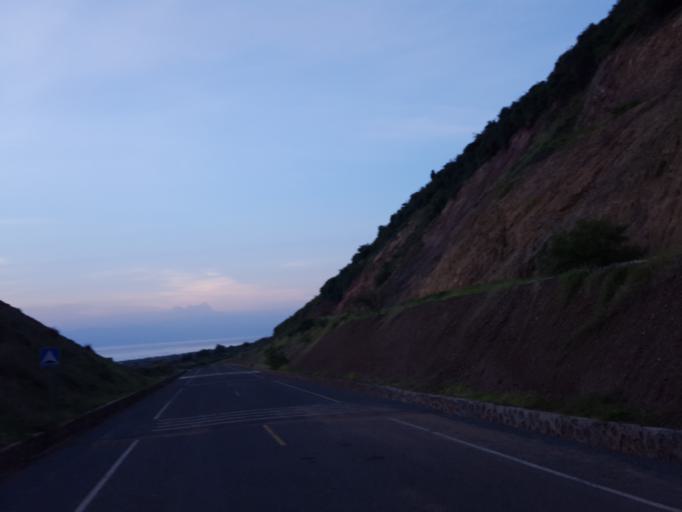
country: UG
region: Western Region
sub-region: Kibale District
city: Kagadi
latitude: 1.2492
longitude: 30.7584
